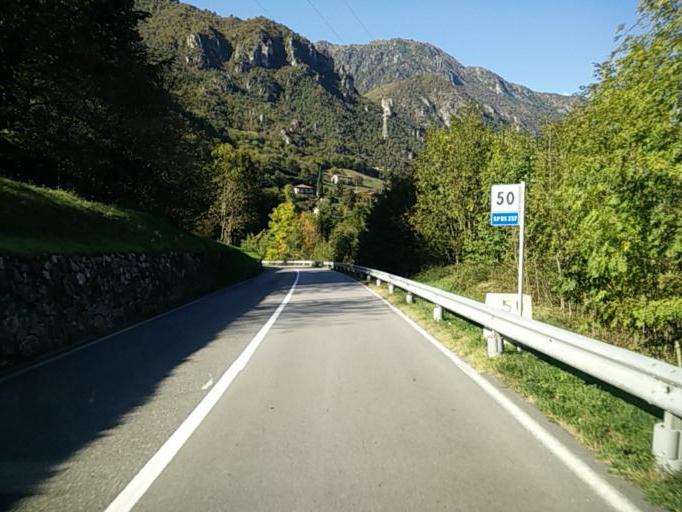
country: IT
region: Lombardy
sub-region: Provincia di Brescia
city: Anfo
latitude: 45.7828
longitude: 10.5023
